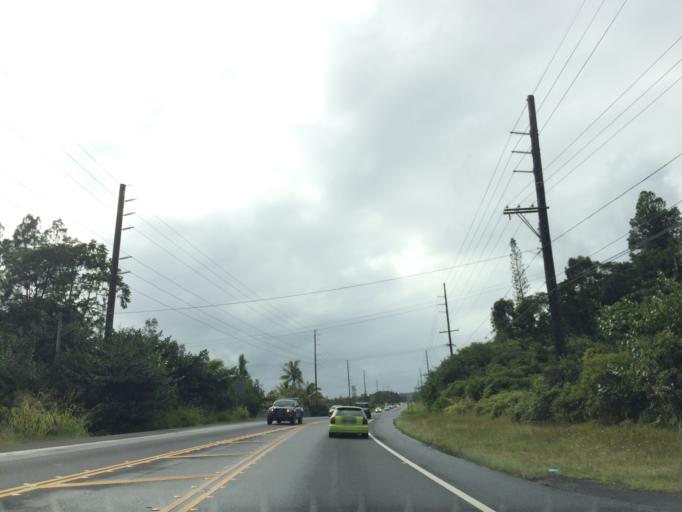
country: US
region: Hawaii
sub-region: Hawaii County
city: Ainaloa
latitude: 19.5417
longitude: -154.9738
